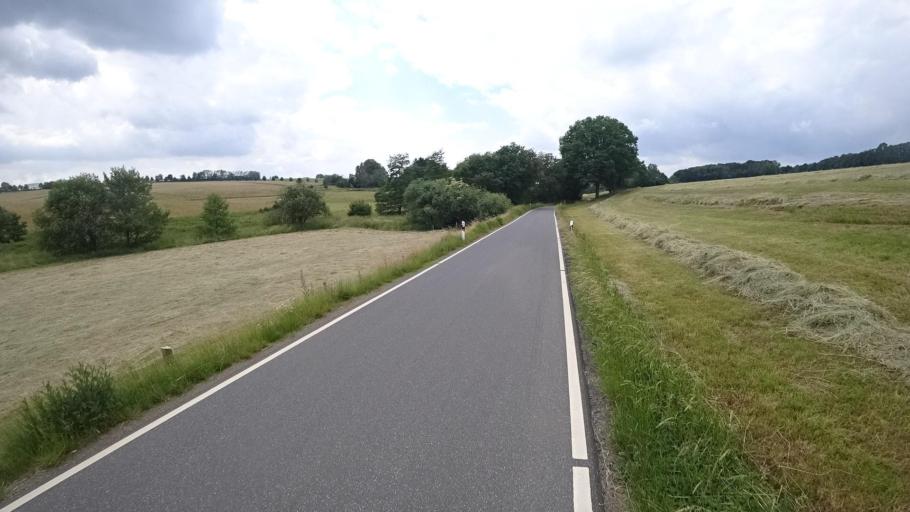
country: DE
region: Rheinland-Pfalz
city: Volkerzen
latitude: 50.7178
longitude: 7.6799
